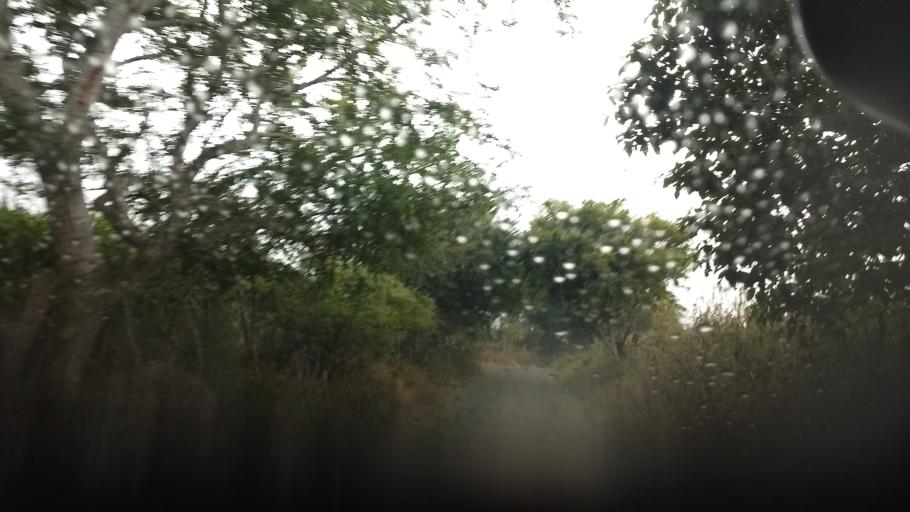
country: MX
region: Jalisco
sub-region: Tonila
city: San Marcos
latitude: 19.4591
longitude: -103.5207
